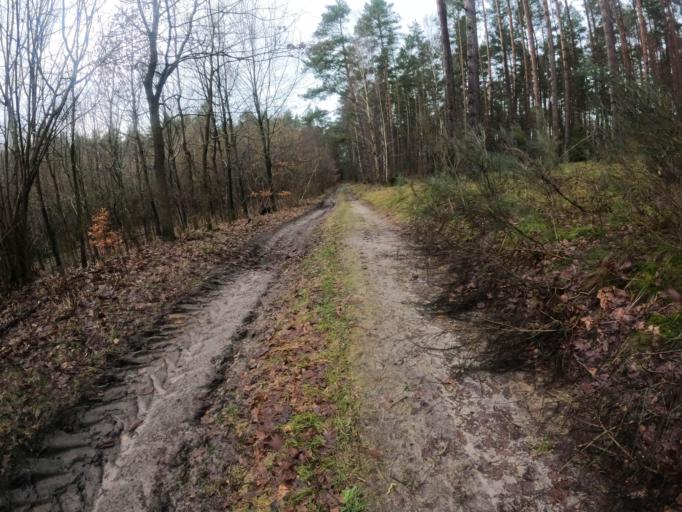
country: PL
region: West Pomeranian Voivodeship
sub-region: Powiat slawienski
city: Slawno
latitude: 54.2433
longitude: 16.6905
